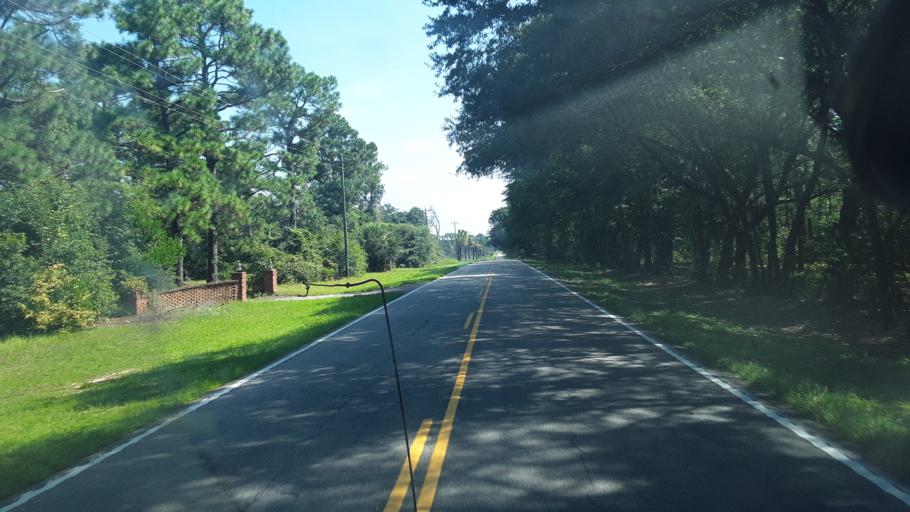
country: US
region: South Carolina
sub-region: Hampton County
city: Varnville
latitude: 32.8907
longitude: -81.0164
